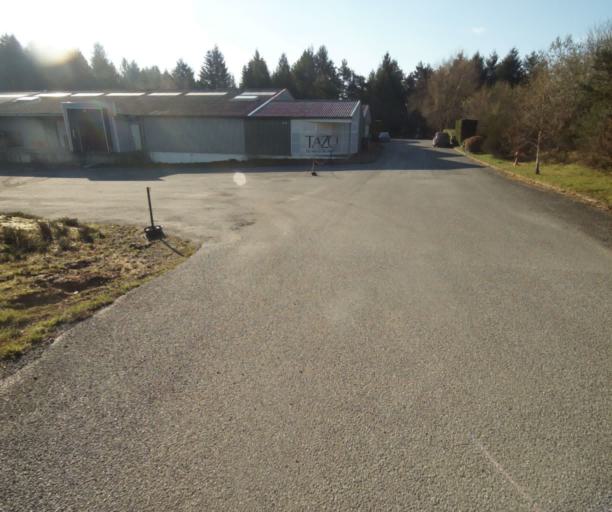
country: FR
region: Limousin
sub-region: Departement de la Correze
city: Correze
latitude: 45.3366
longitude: 1.9161
